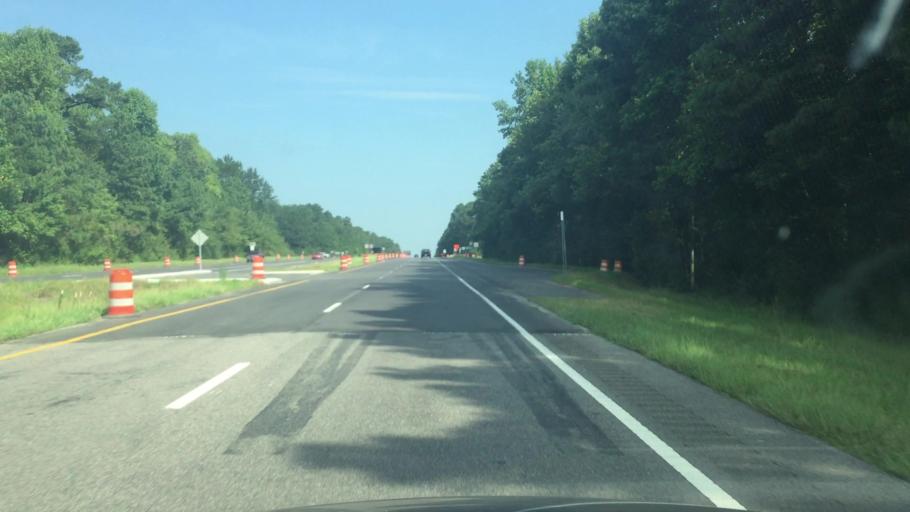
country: US
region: North Carolina
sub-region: Robeson County
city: Fairmont
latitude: 34.4784
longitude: -78.9867
